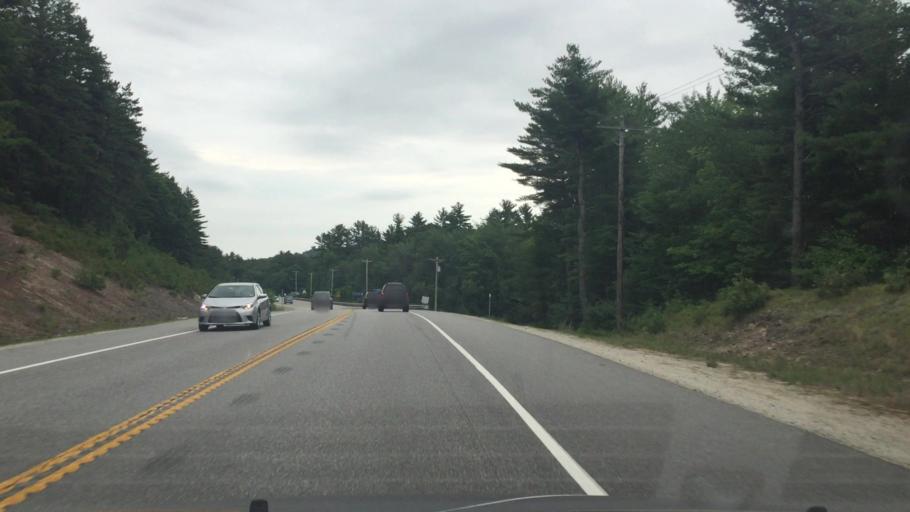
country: US
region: New Hampshire
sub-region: Carroll County
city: Ossipee
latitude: 43.6385
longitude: -71.0586
